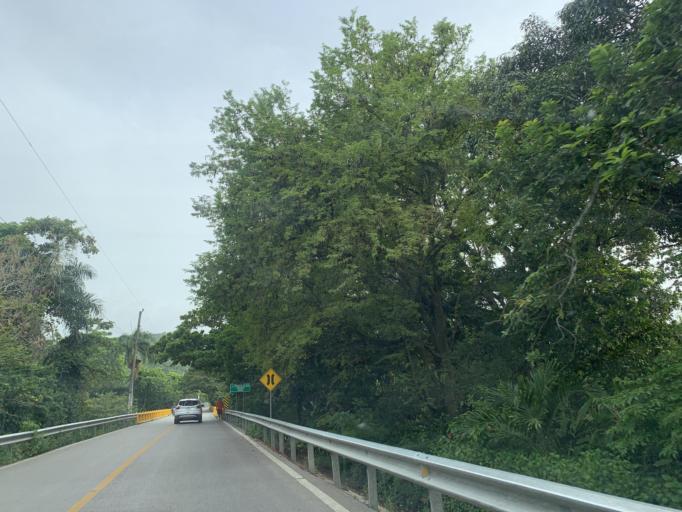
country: DO
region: Santiago
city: Pedro Garcia
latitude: 19.6992
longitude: -70.6238
